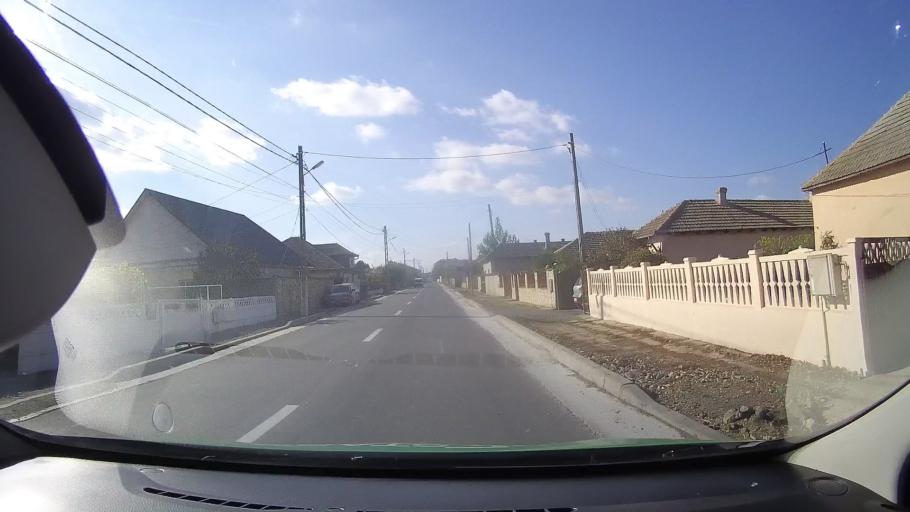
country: RO
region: Constanta
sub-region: Comuna Cogealac
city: Cogealac
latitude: 44.5585
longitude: 28.5689
